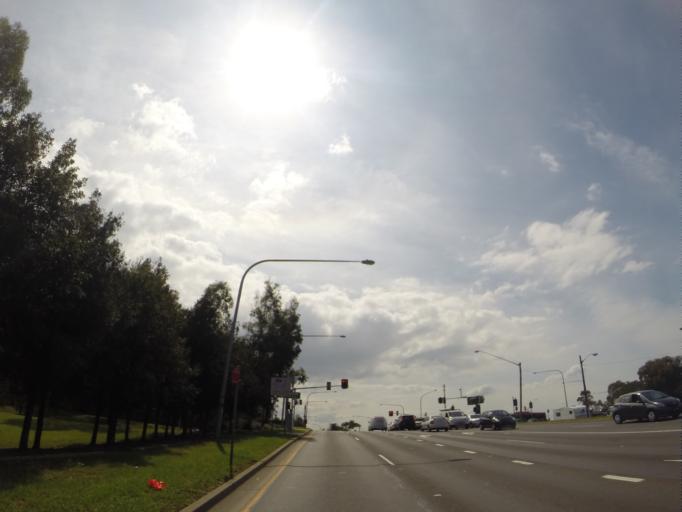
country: AU
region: New South Wales
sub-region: Bankstown
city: Bankstown
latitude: -33.9073
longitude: 151.0403
